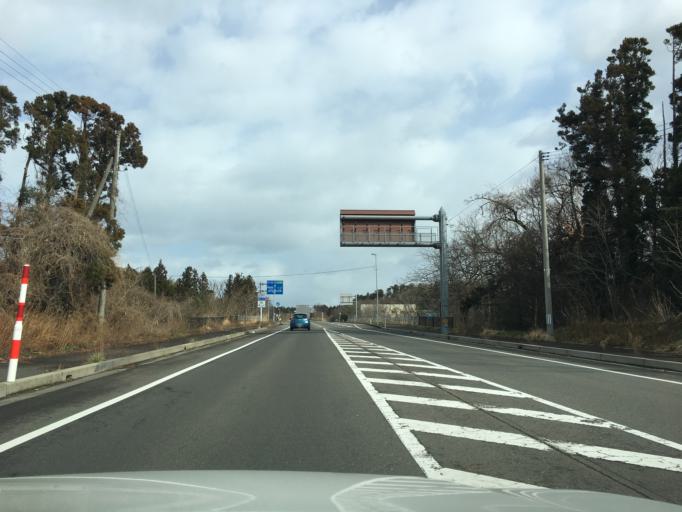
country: JP
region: Yamagata
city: Yuza
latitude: 39.2536
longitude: 139.9269
